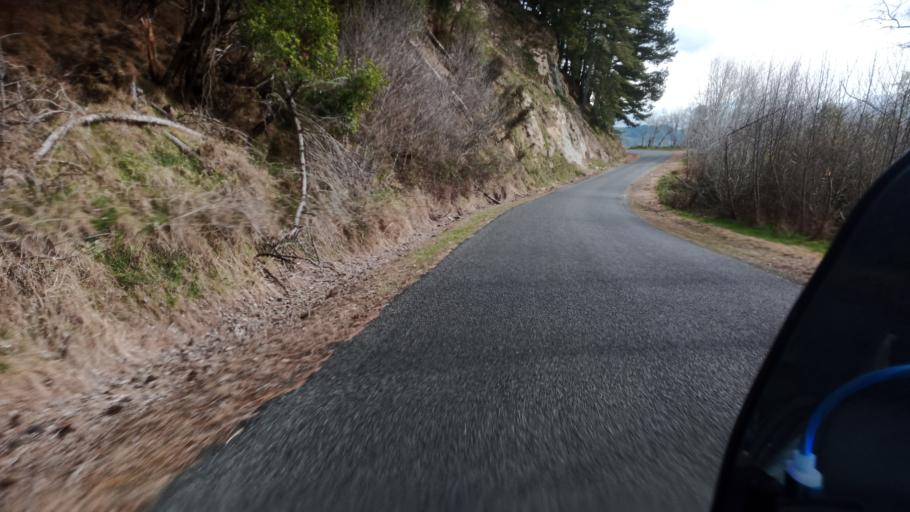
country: NZ
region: Hawke's Bay
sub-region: Wairoa District
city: Wairoa
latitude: -38.7734
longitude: 177.4229
